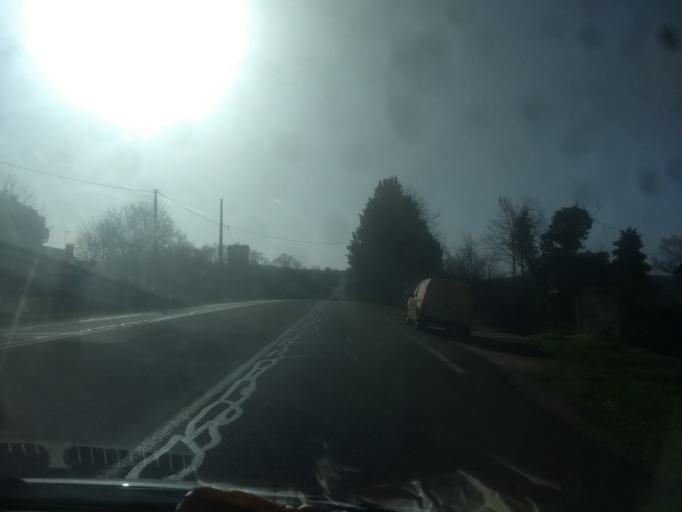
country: FR
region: Centre
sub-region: Departement du Cher
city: Orval
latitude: 46.7749
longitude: 2.4322
